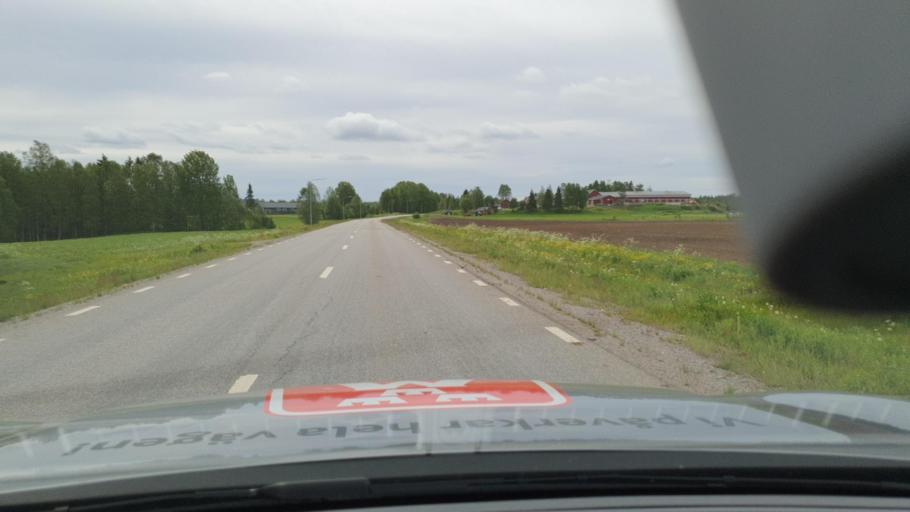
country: SE
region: Norrbotten
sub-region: Kalix Kommun
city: Kalix
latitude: 65.9736
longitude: 23.4607
